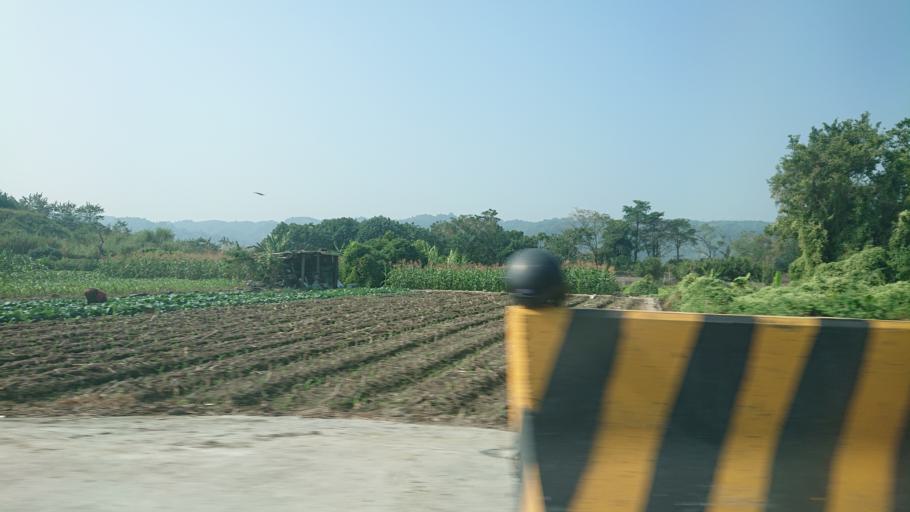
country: TW
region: Taiwan
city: Lugu
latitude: 23.7626
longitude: 120.6613
